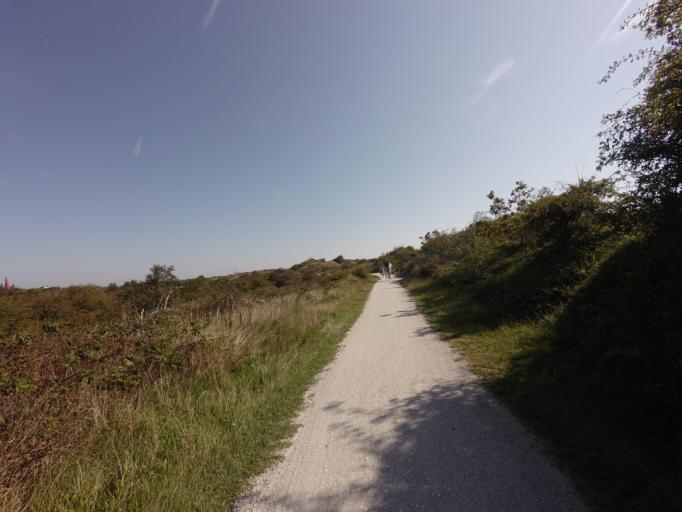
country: NL
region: Friesland
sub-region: Gemeente Schiermonnikoog
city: Schiermonnikoog
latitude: 53.4794
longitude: 6.1440
